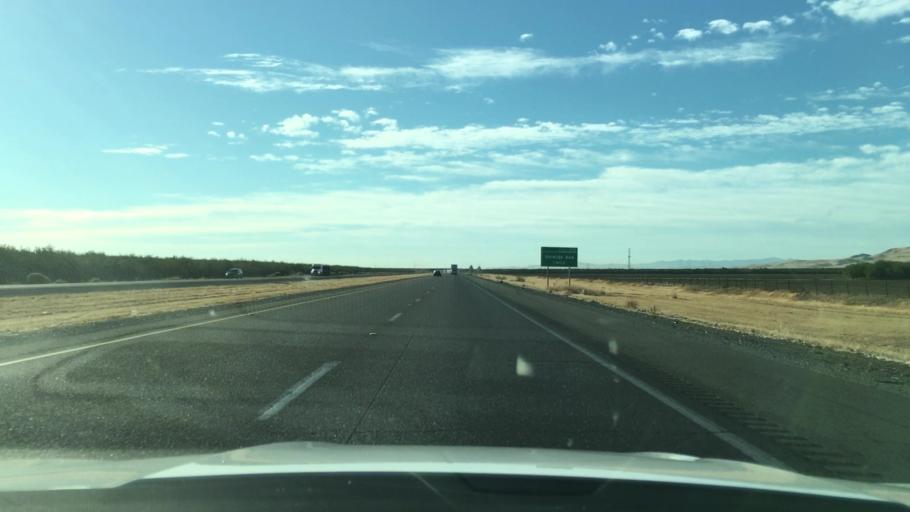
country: US
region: California
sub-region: Merced County
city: South Dos Palos
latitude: 36.7954
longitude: -120.7367
